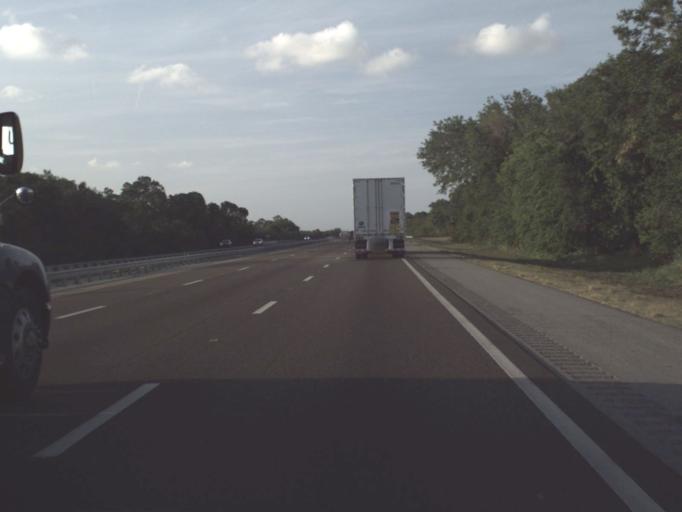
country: US
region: Florida
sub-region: Brevard County
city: Port Saint John
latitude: 28.5247
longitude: -80.8516
